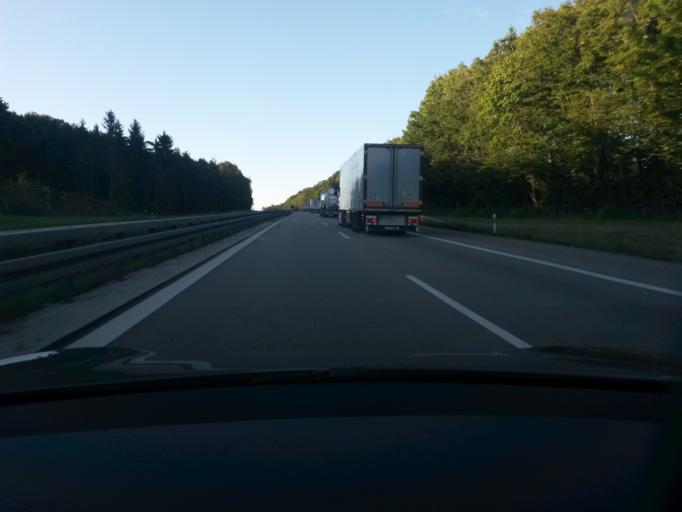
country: DE
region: Bavaria
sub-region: Upper Palatinate
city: Brunn
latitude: 49.1231
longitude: 11.8712
